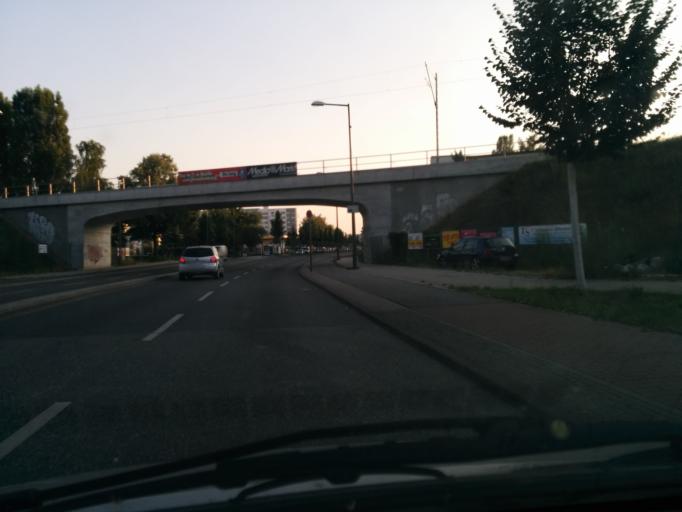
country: DE
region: Berlin
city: Adlershof
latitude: 52.4364
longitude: 13.5613
